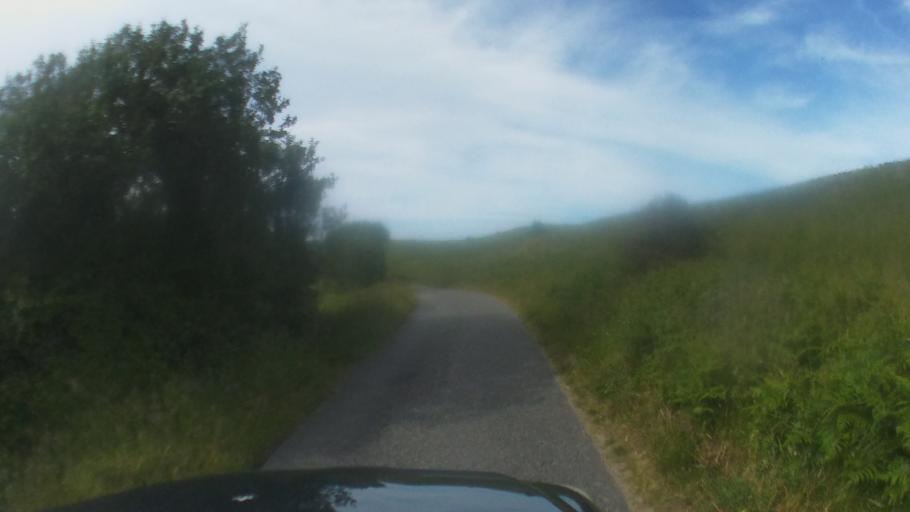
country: IE
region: Leinster
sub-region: Loch Garman
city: Castlebridge
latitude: 52.3929
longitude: -6.3628
